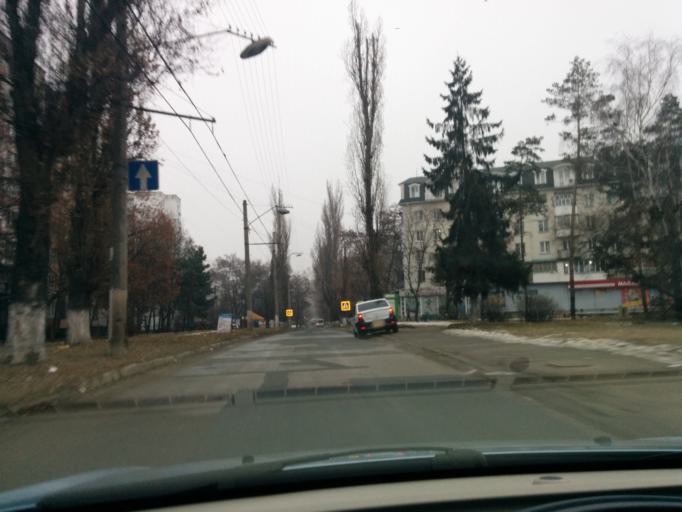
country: MD
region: Chisinau
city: Chisinau
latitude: 47.0013
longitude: 28.8605
